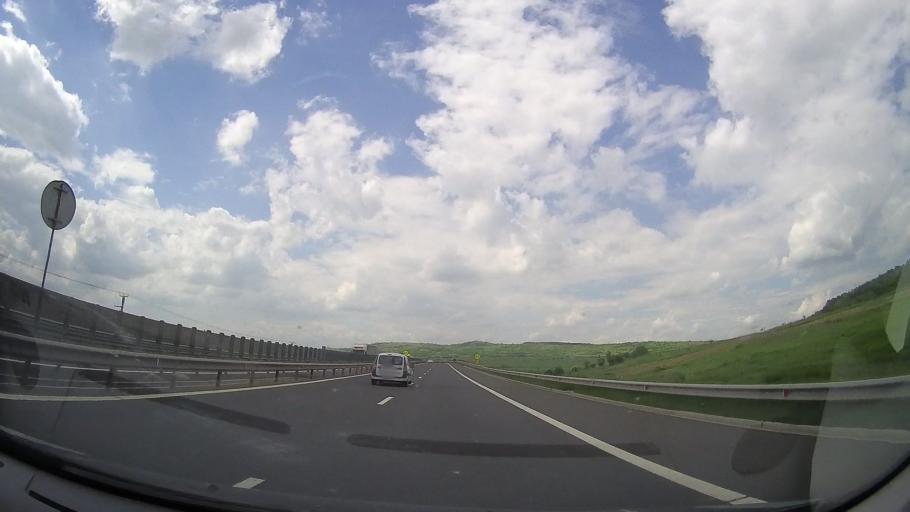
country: RO
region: Sibiu
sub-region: Comuna Apoldu de Jos
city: Apoldu de Jos
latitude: 45.8819
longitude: 23.8563
